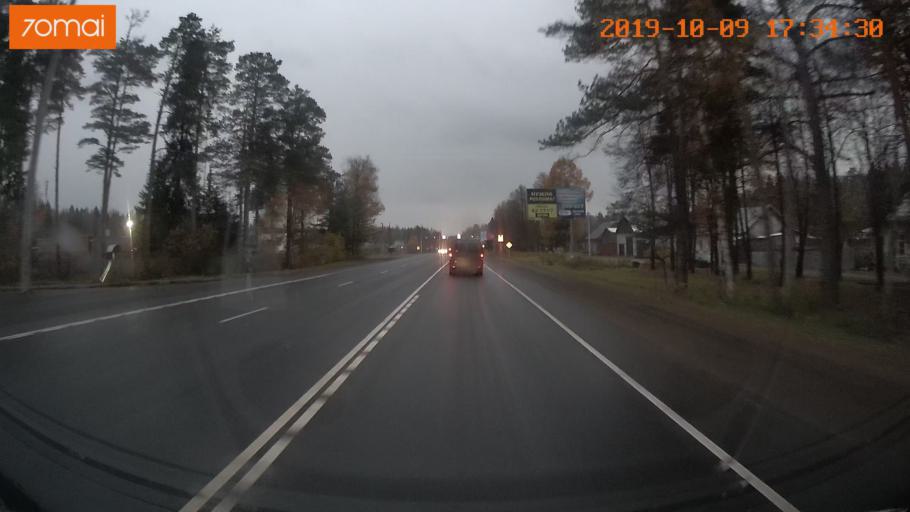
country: RU
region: Ivanovo
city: Bogorodskoye
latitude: 57.1060
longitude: 41.0110
